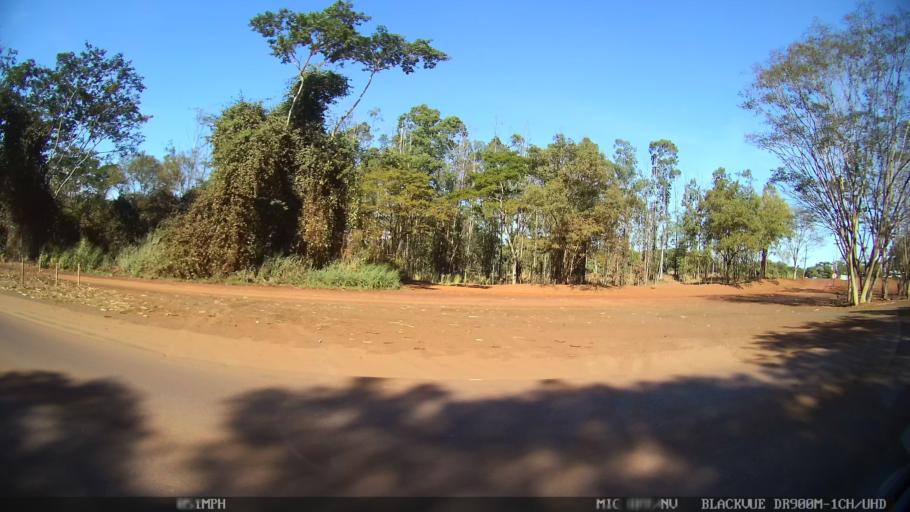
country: BR
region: Sao Paulo
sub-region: Barretos
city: Barretos
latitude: -20.4577
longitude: -48.4624
